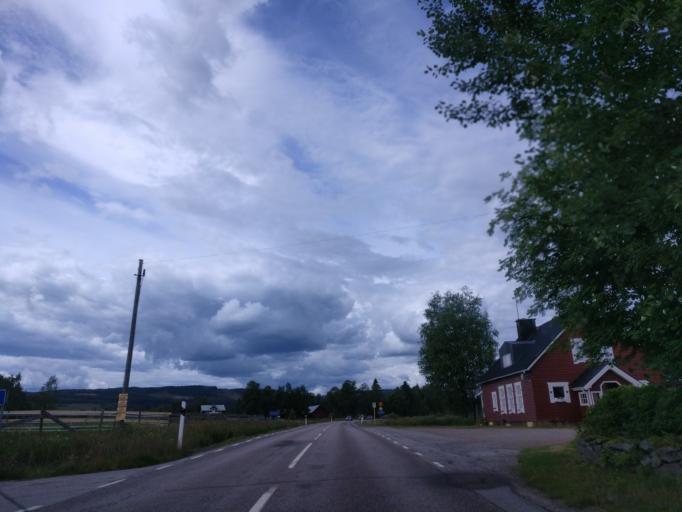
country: SE
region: Vaermland
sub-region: Hagfors Kommun
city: Ekshaerad
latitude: 60.1530
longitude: 13.4313
